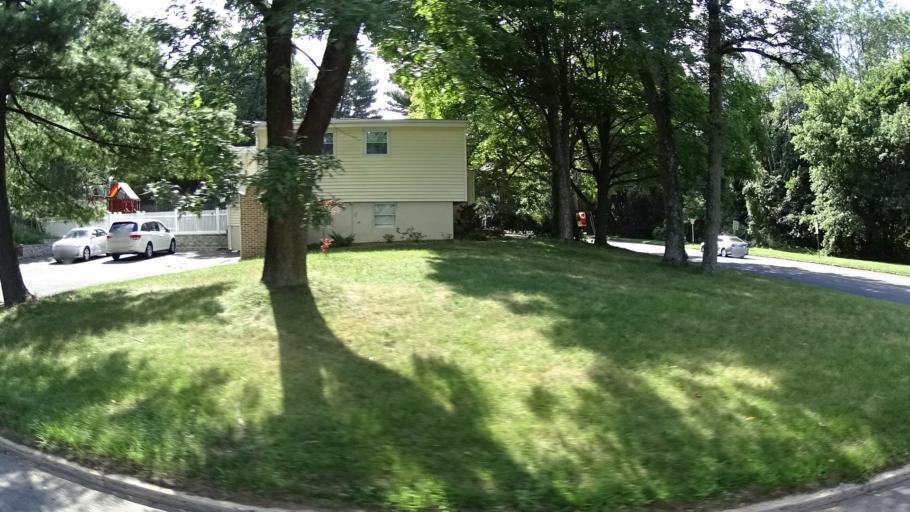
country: US
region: New Jersey
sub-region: Morris County
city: Chatham
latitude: 40.7331
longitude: -74.3727
